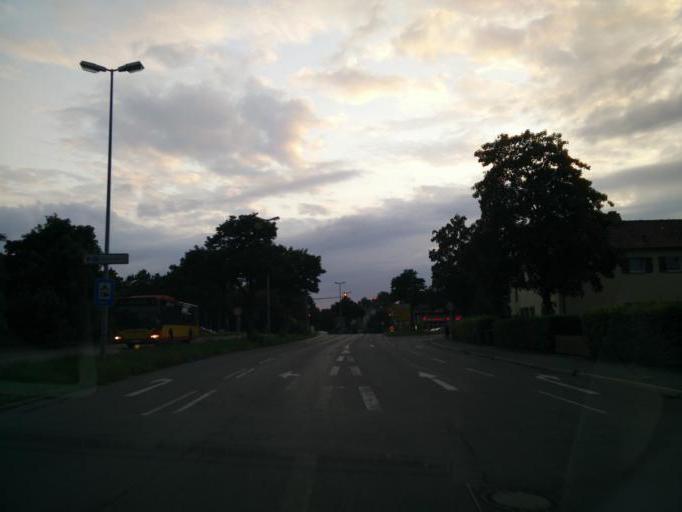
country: DE
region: Baden-Wuerttemberg
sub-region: Tuebingen Region
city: Tuebingen
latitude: 48.5217
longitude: 9.0440
